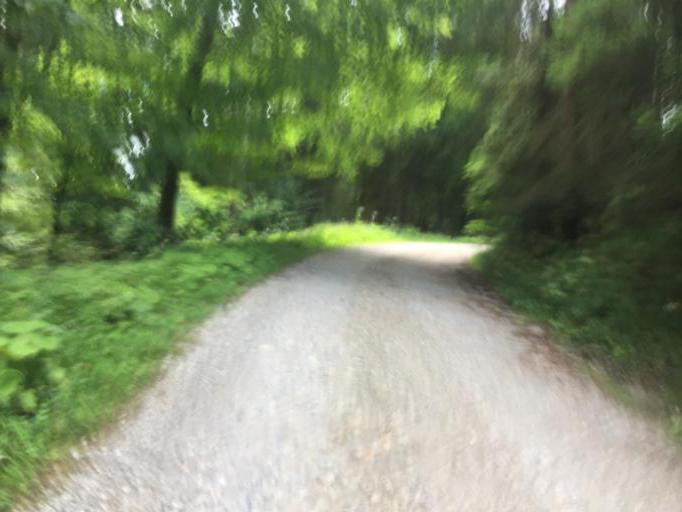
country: CH
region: Bern
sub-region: Thun District
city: Wattenwil
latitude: 46.7585
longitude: 7.4808
